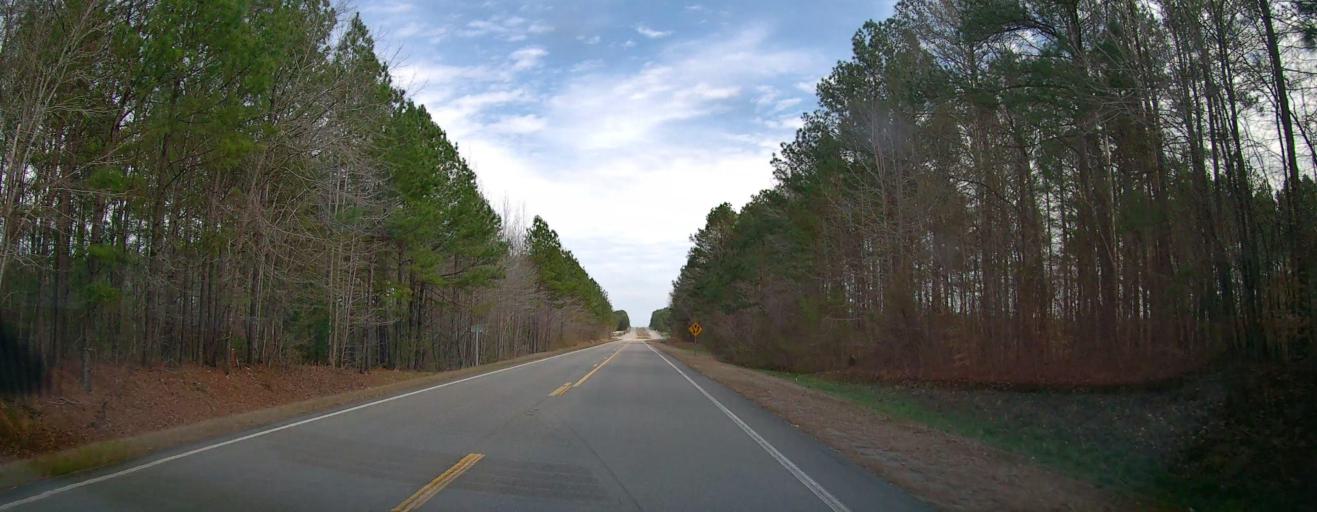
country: US
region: Alabama
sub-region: Marion County
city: Winfield
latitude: 33.9344
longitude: -87.7136
